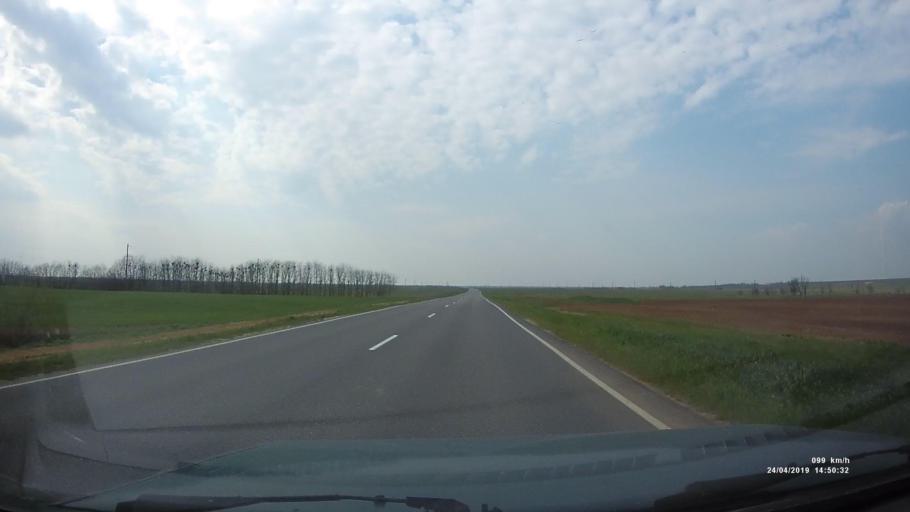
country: RU
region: Rostov
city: Remontnoye
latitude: 46.5180
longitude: 43.7176
